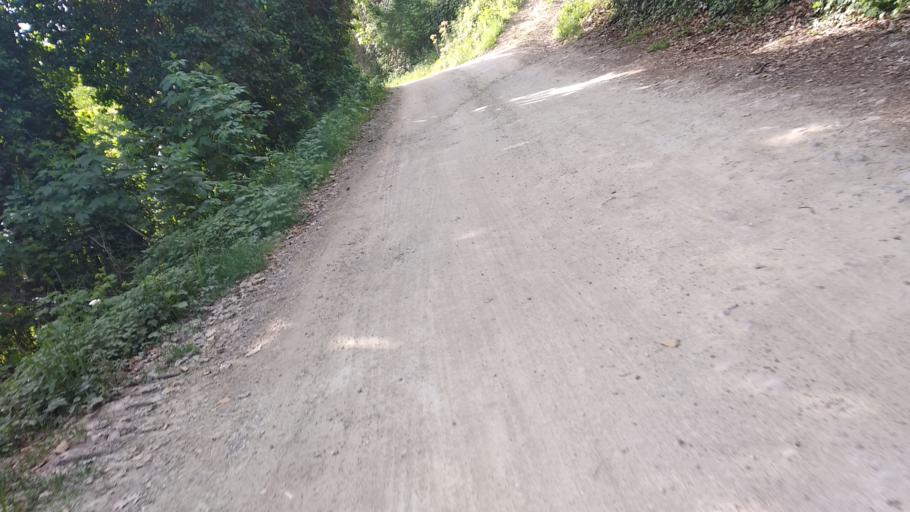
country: IT
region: Emilia-Romagna
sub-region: Provincia di Ravenna
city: Fognano
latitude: 44.2261
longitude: 11.7440
